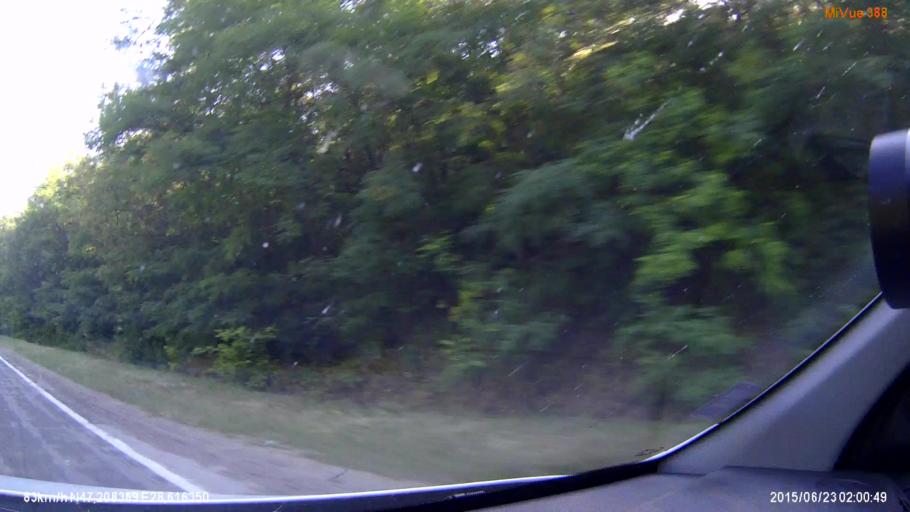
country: MD
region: Straseni
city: Straseni
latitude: 47.2088
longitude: 28.6165
